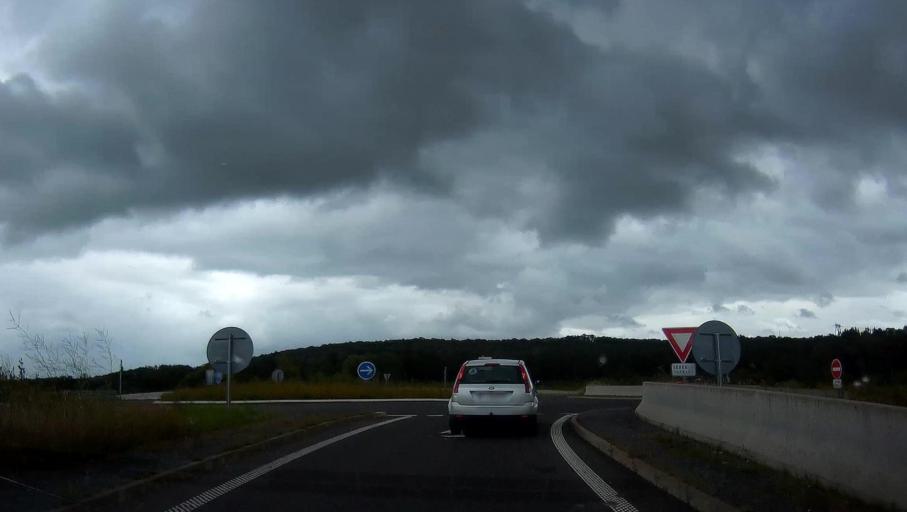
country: FR
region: Champagne-Ardenne
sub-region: Departement des Ardennes
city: Tournes
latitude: 49.7650
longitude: 4.6417
